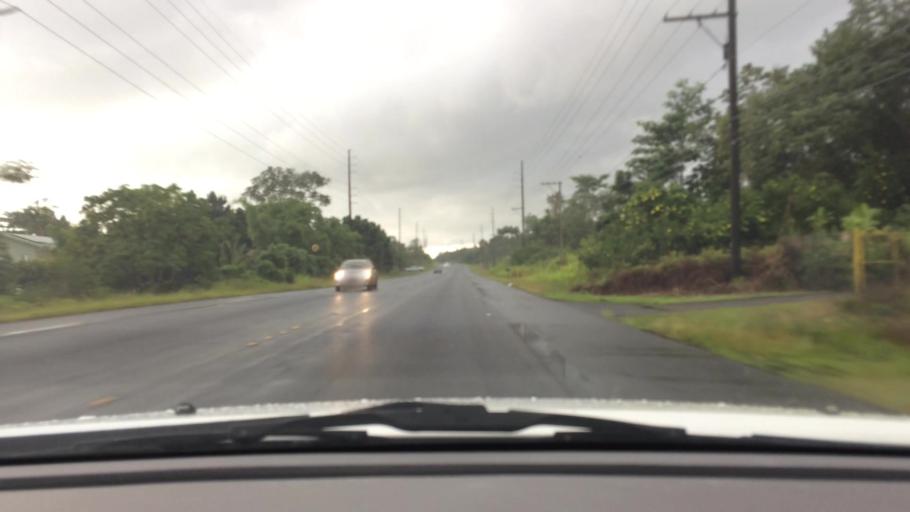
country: US
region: Hawaii
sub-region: Hawaii County
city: Ainaloa
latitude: 19.5516
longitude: -154.9838
